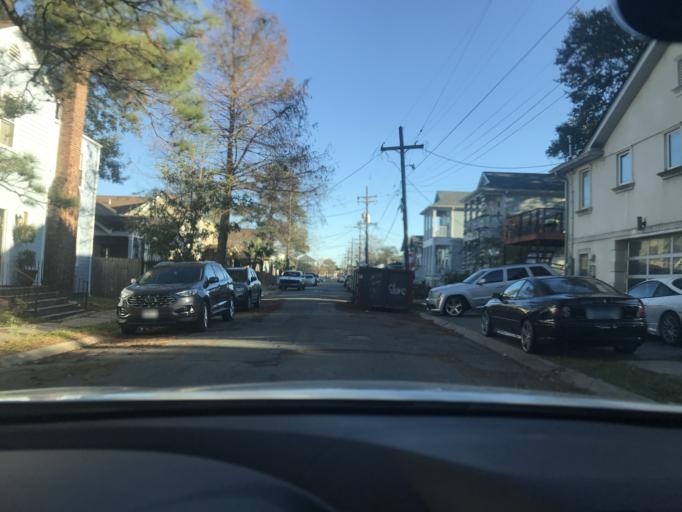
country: US
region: Louisiana
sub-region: Orleans Parish
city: New Orleans
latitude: 29.9544
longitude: -90.1064
